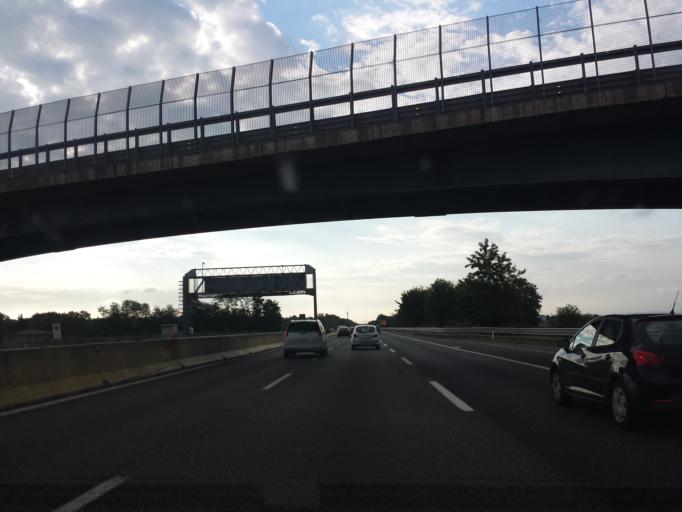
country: IT
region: Lombardy
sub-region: Citta metropolitana di Milano
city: Cantalupo
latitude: 45.5898
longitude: 8.9766
